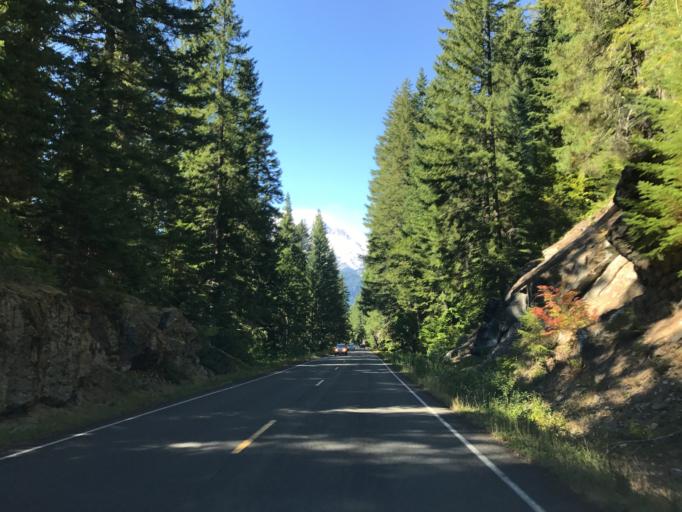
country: US
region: Washington
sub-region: Pierce County
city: Buckley
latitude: 46.7279
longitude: -121.6076
